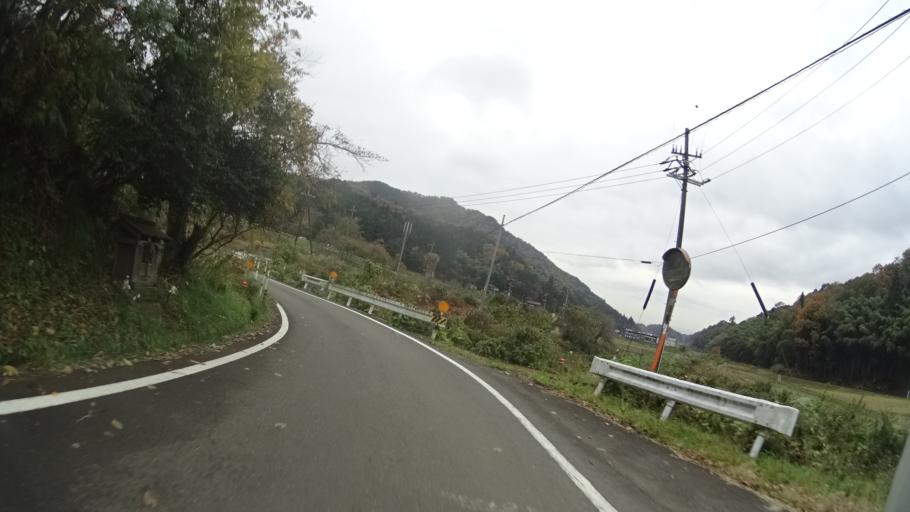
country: JP
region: Kyoto
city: Maizuru
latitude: 35.4869
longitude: 135.4638
